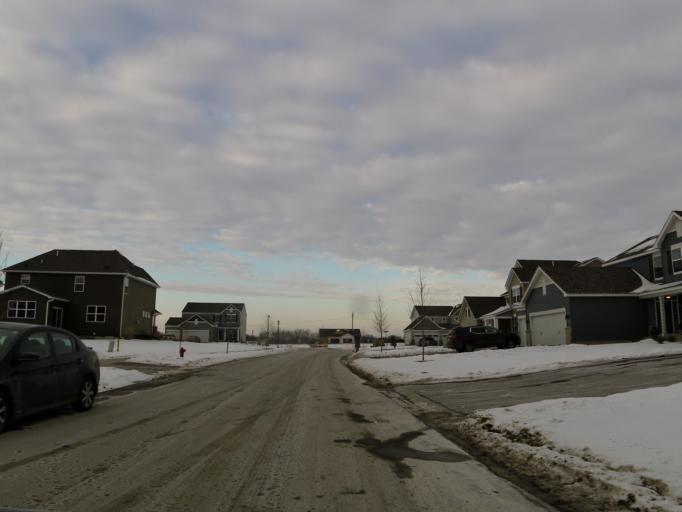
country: US
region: Minnesota
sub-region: Washington County
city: Lake Elmo
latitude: 44.9536
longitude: -92.8805
